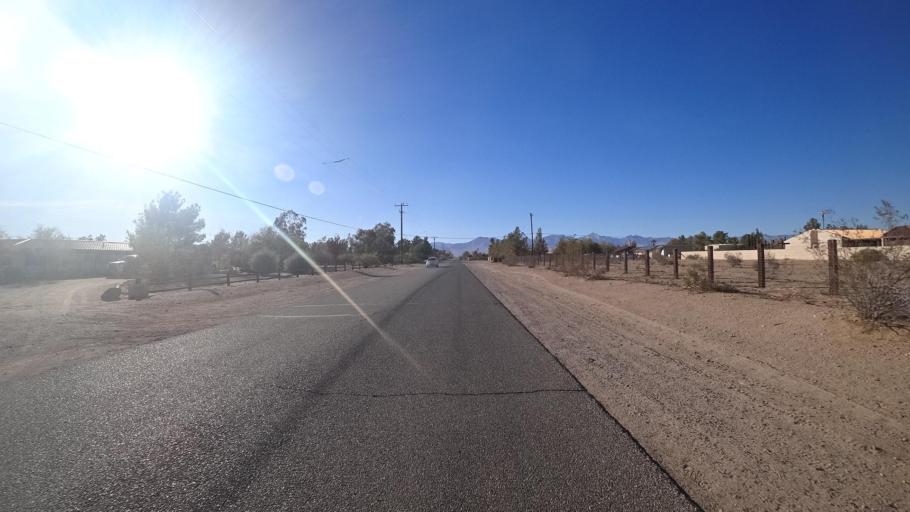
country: US
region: California
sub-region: Kern County
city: Ridgecrest
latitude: 35.6444
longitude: -117.7002
